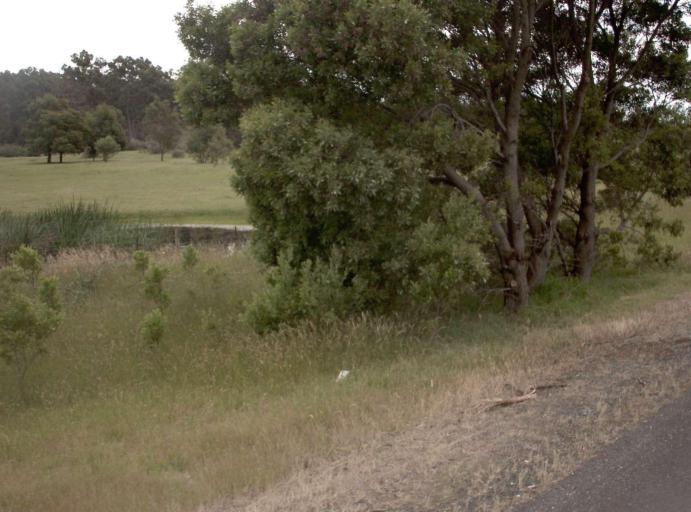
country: AU
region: Victoria
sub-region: Wellington
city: Sale
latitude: -38.2425
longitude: 147.0550
